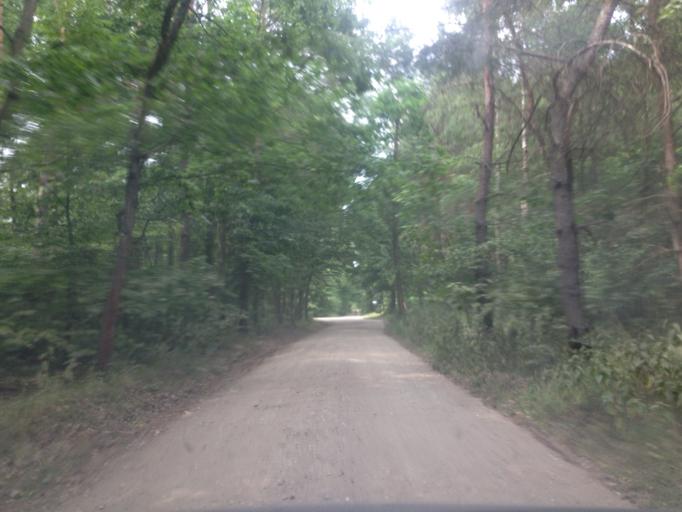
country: PL
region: Kujawsko-Pomorskie
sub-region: Powiat golubsko-dobrzynski
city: Radomin
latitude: 53.1488
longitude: 19.1382
